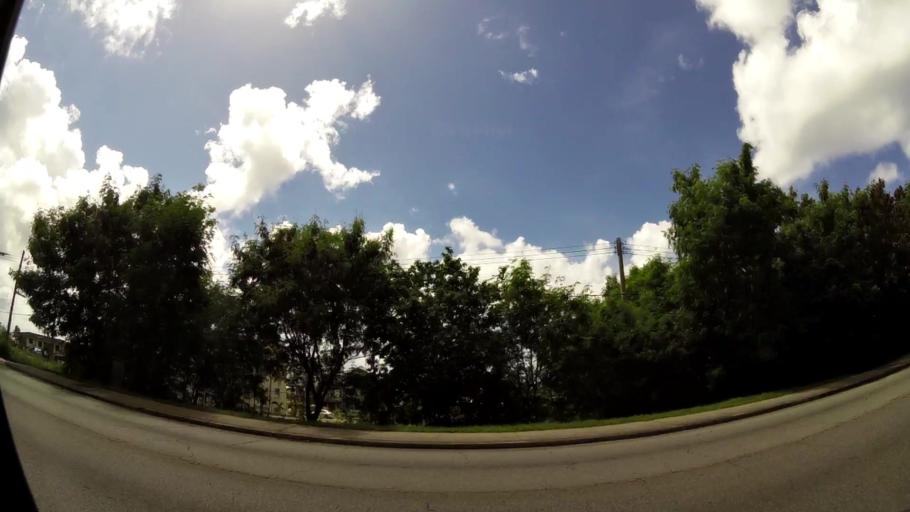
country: BB
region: Saint Michael
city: Bridgetown
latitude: 13.1363
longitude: -59.6251
